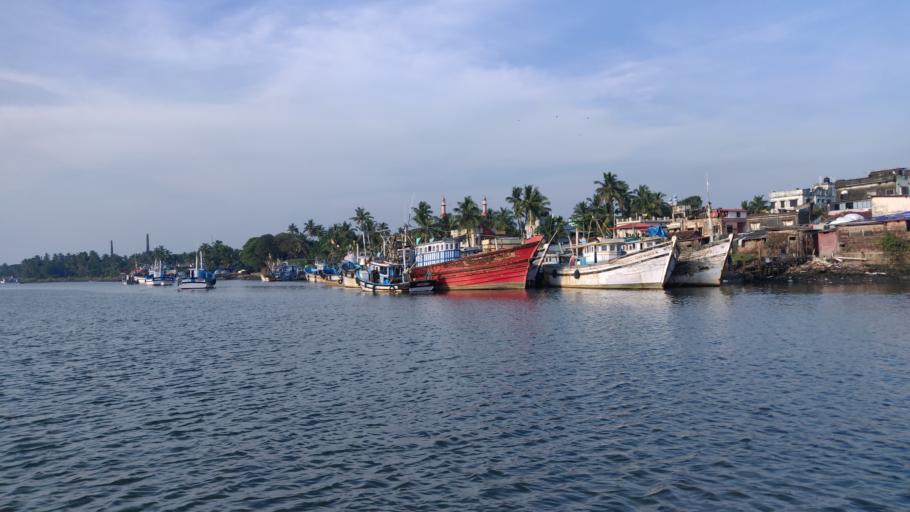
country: IN
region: Karnataka
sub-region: Dakshina Kannada
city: Mangalore
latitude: 12.8737
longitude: 74.8285
